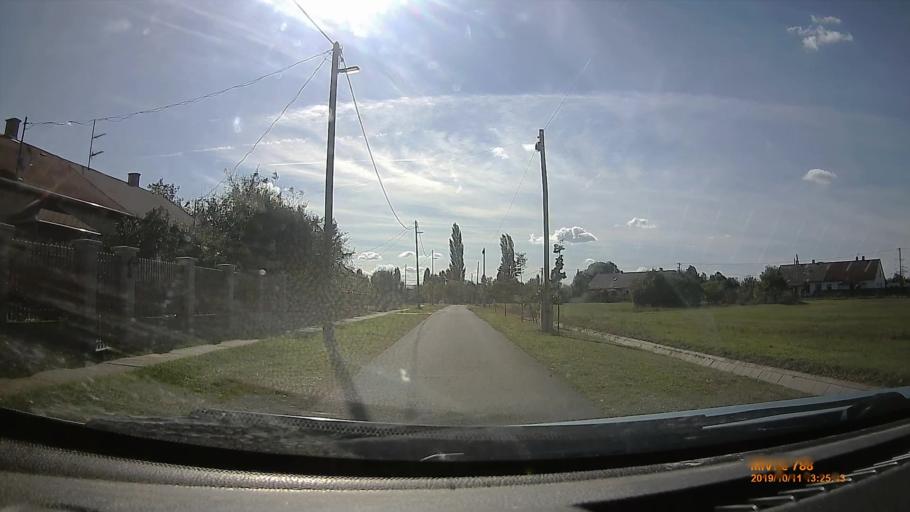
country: HU
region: Hajdu-Bihar
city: Balmazujvaros
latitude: 47.5408
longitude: 21.3141
